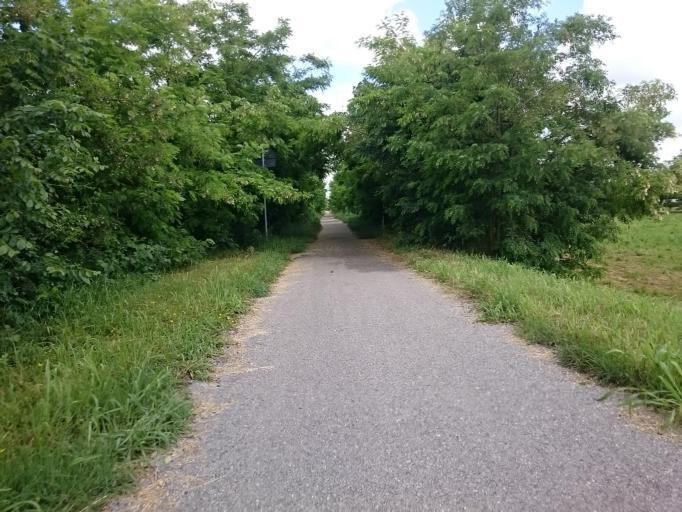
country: IT
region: Veneto
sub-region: Provincia di Padova
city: Piazzola sul Brenta
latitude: 45.5221
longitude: 11.7626
